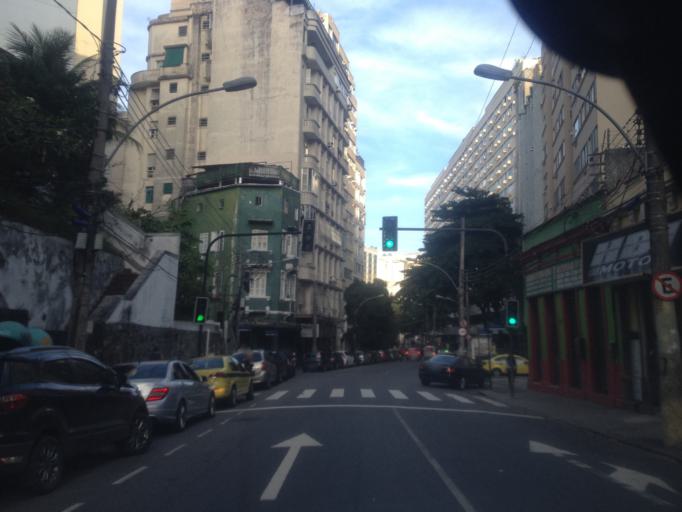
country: BR
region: Rio de Janeiro
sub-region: Rio De Janeiro
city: Rio de Janeiro
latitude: -22.9654
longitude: -43.1889
